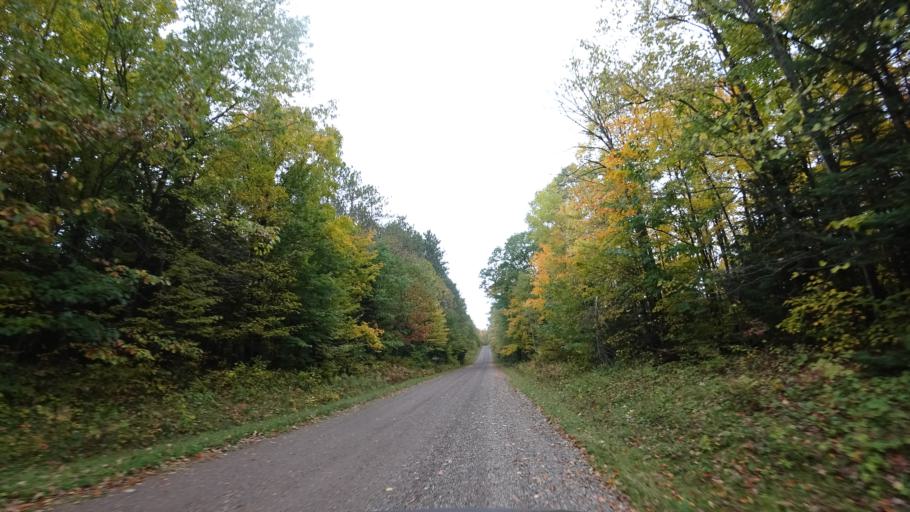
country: US
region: Wisconsin
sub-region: Sawyer County
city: Little Round Lake
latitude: 45.9627
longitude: -90.9802
